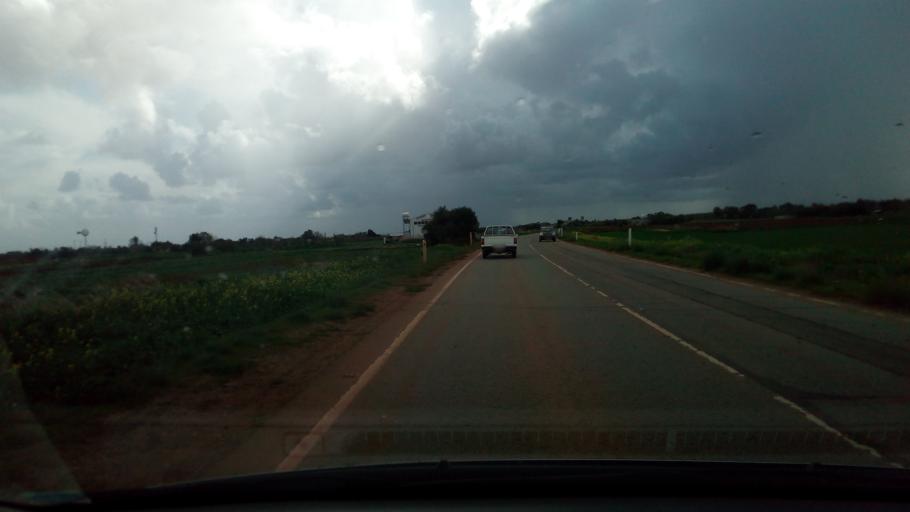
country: CY
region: Ammochostos
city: Liopetri
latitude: 34.9845
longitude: 33.8947
